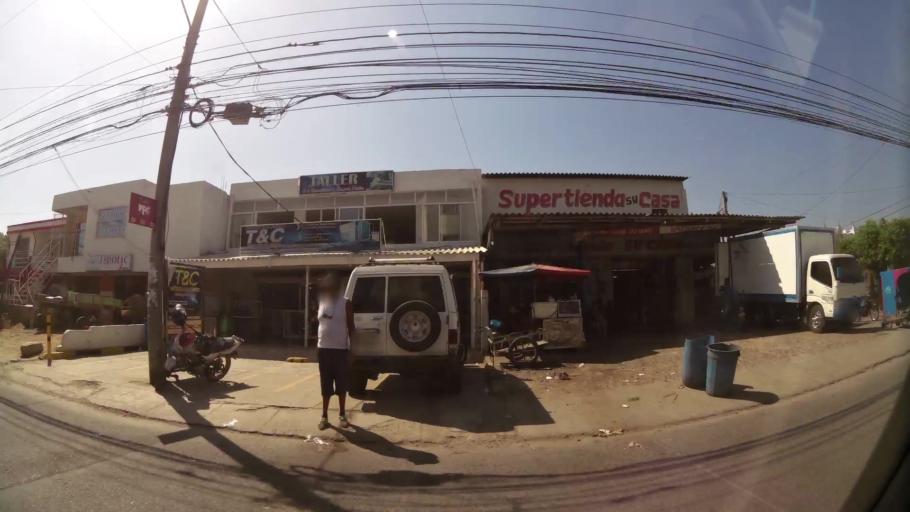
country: CO
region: Bolivar
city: Cartagena
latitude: 10.3789
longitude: -75.4731
